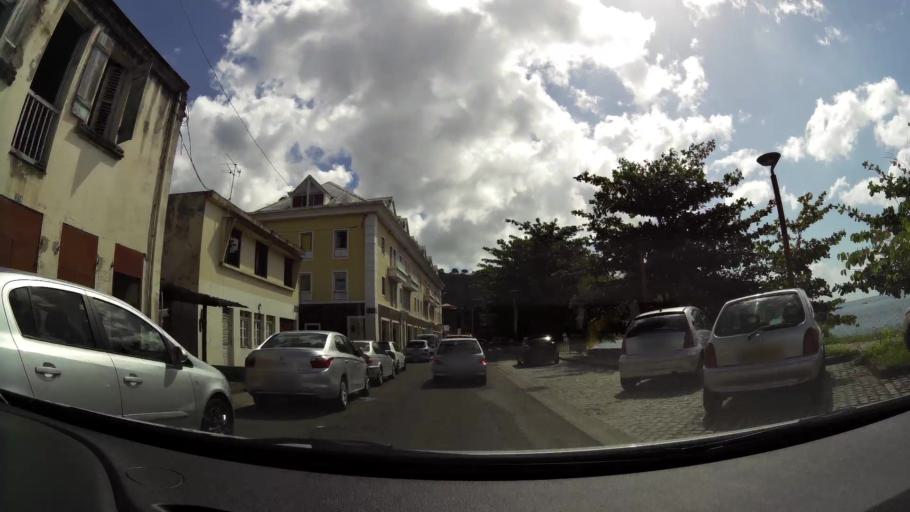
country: MQ
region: Martinique
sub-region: Martinique
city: Saint-Pierre
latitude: 14.7466
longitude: -61.1772
